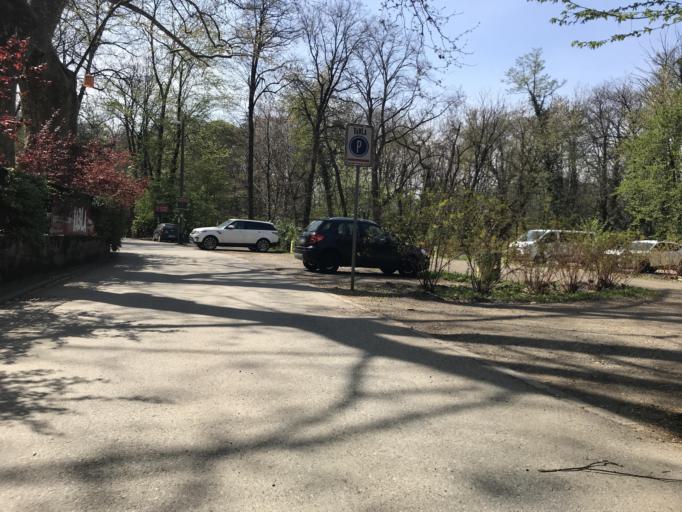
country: CH
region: Ticino
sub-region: Lugano District
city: Montagnola
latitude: 45.9895
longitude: 8.9222
